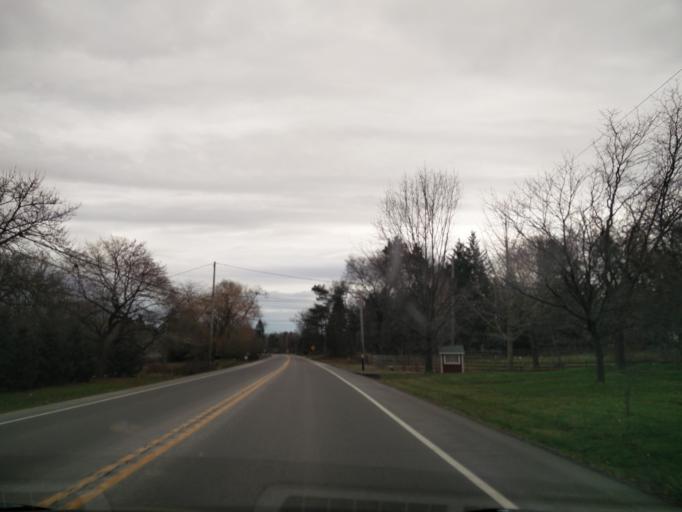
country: US
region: New York
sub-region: Tompkins County
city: Northwest Ithaca
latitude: 42.4754
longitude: -76.5548
